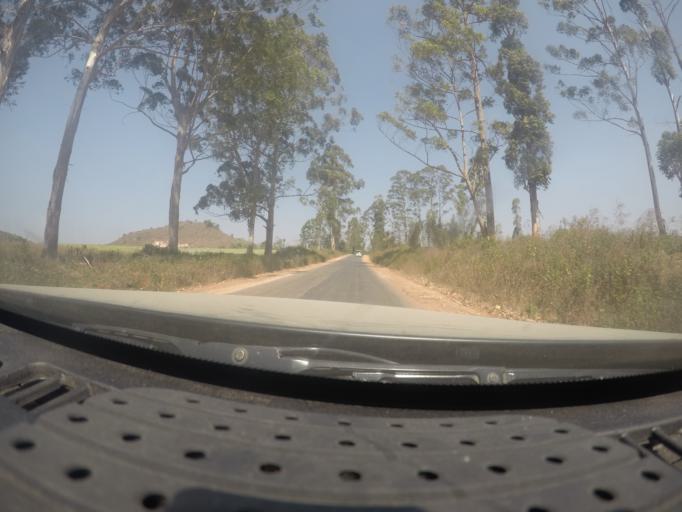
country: MM
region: Shan
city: Taunggyi
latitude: 20.8741
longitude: 96.5815
